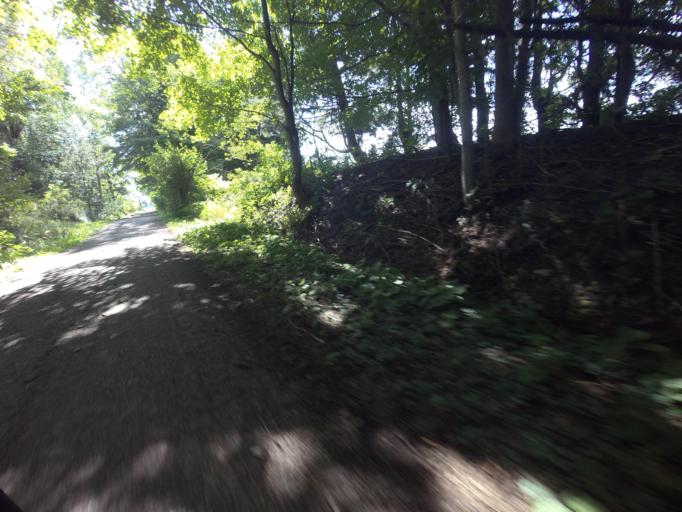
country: CA
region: Ontario
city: Huron East
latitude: 43.6869
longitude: -81.3156
